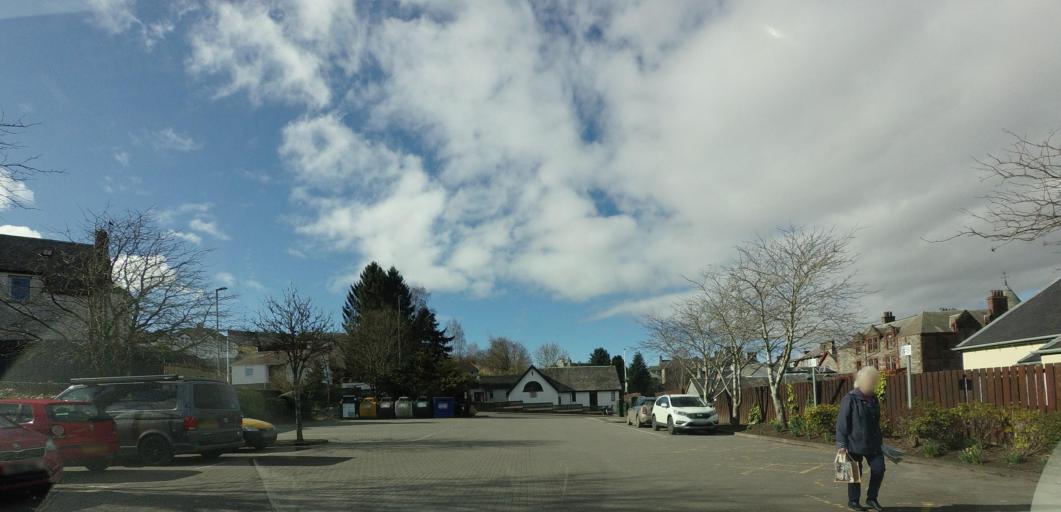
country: GB
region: Scotland
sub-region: Perth and Kinross
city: Aberfeldy
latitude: 56.6200
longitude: -3.8620
